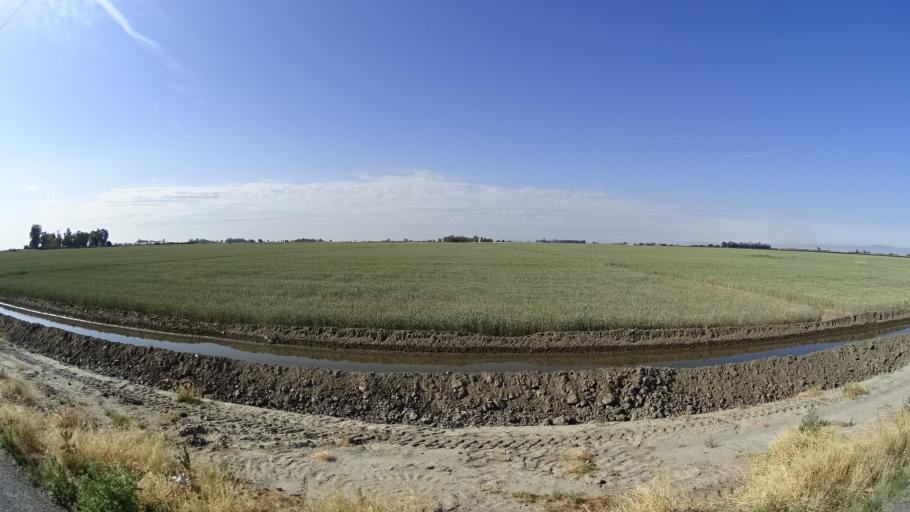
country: US
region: California
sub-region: Kings County
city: Stratford
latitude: 36.2259
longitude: -119.7923
